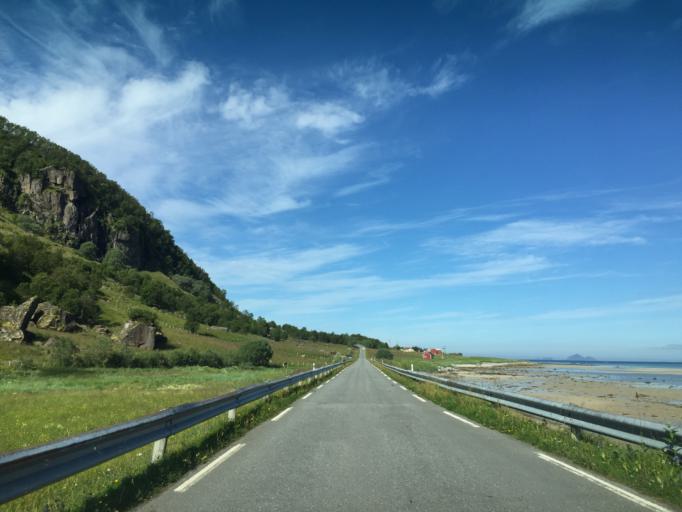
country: NO
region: Nordland
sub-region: Vagan
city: Svolvaer
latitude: 68.3967
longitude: 14.5347
